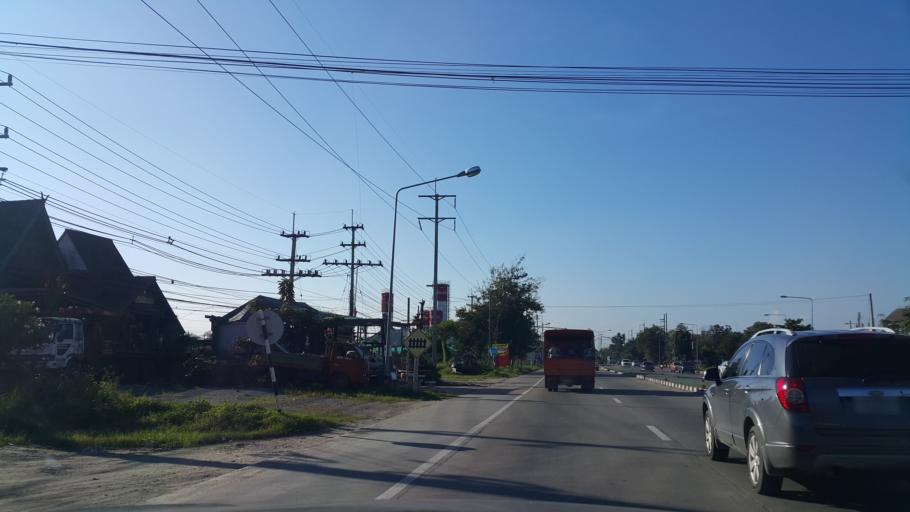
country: TH
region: Lamphun
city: Lamphun
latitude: 18.5526
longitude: 99.0473
